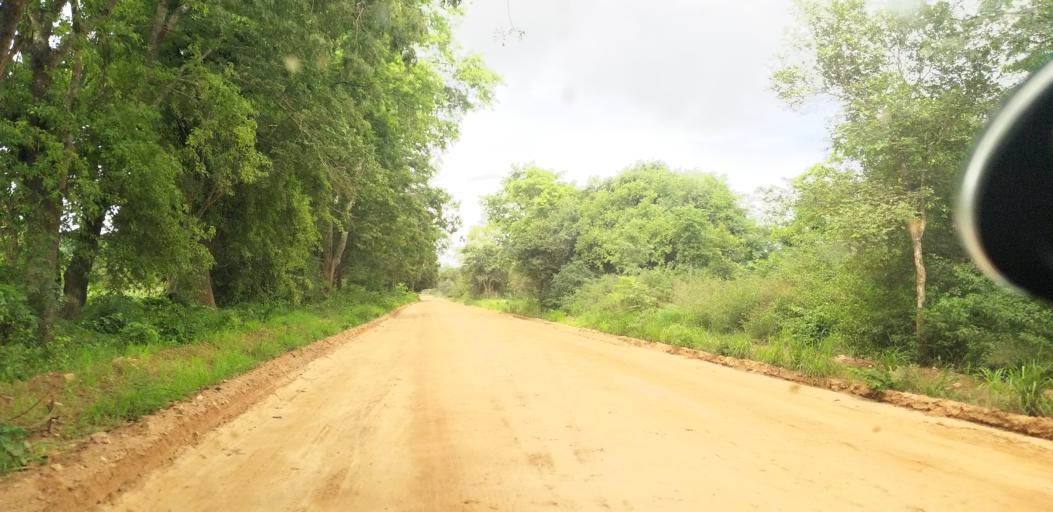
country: ZM
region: Lusaka
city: Lusaka
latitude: -15.1865
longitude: 28.4467
